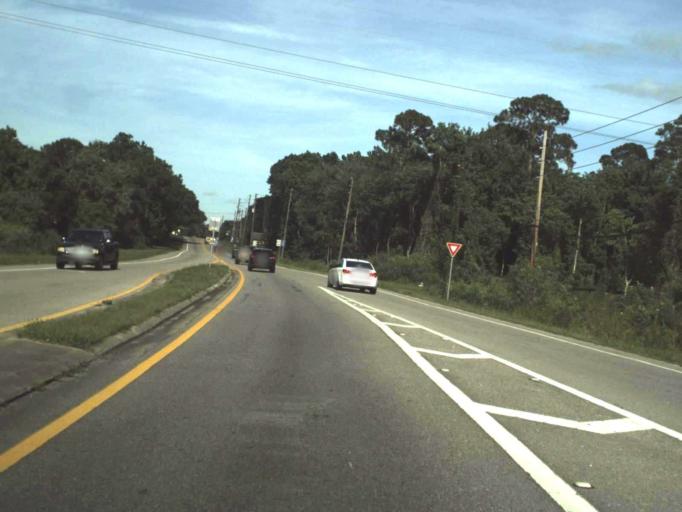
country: US
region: Florida
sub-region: Volusia County
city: DeLand
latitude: 29.0250
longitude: -81.2649
